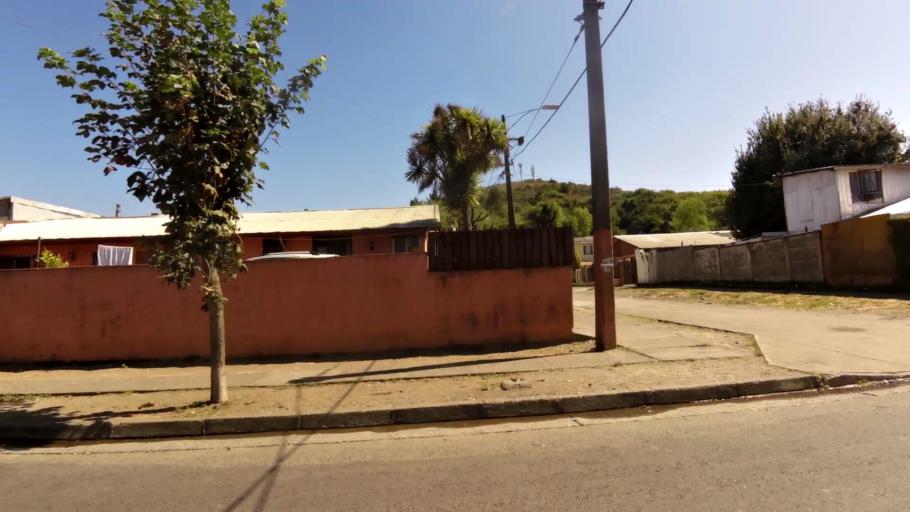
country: CL
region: Biobio
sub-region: Provincia de Concepcion
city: Concepcion
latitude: -36.7945
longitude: -73.0372
